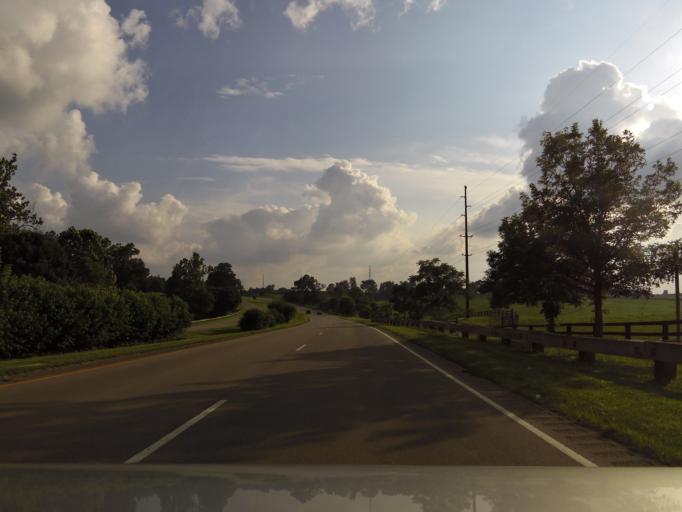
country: US
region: Kentucky
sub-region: Bourbon County
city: Paris
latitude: 38.1781
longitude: -84.3031
